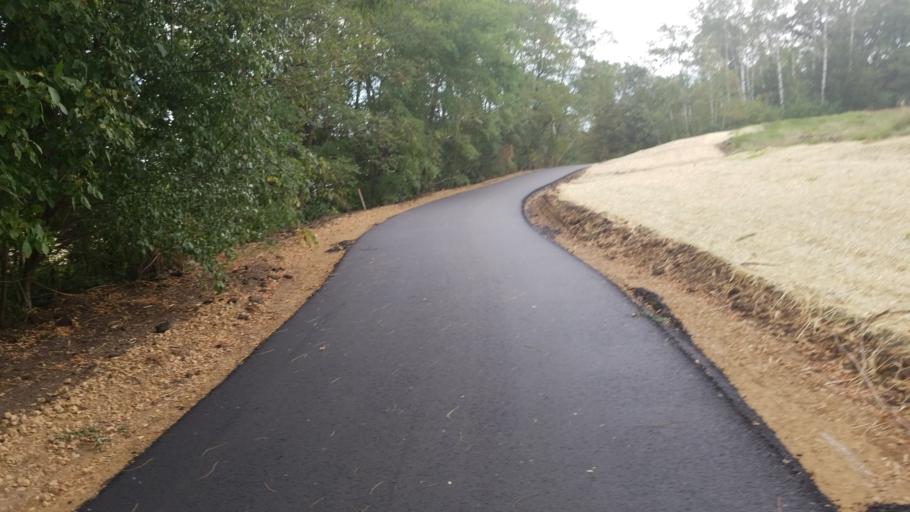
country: US
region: Wisconsin
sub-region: Saint Croix County
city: Hudson
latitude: 44.9704
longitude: -92.7264
